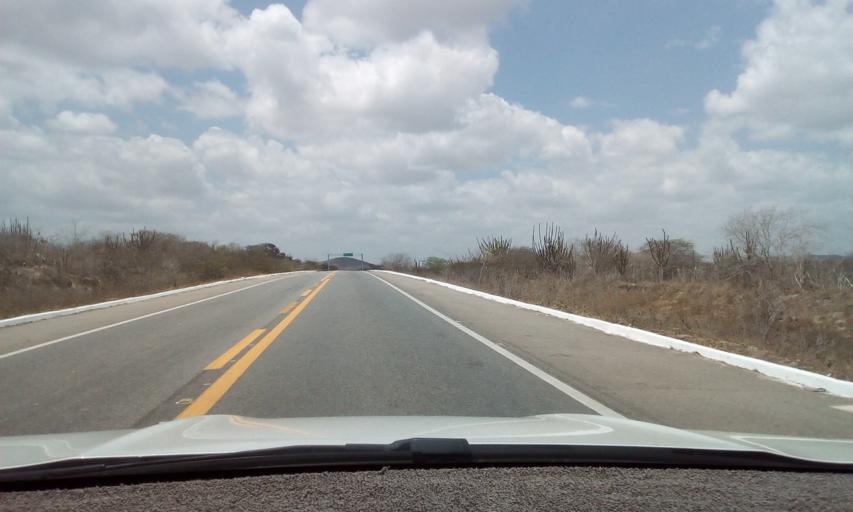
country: BR
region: Pernambuco
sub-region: Taquaritinga Do Norte
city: Taquaritinga do Norte
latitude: -7.7441
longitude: -36.0828
